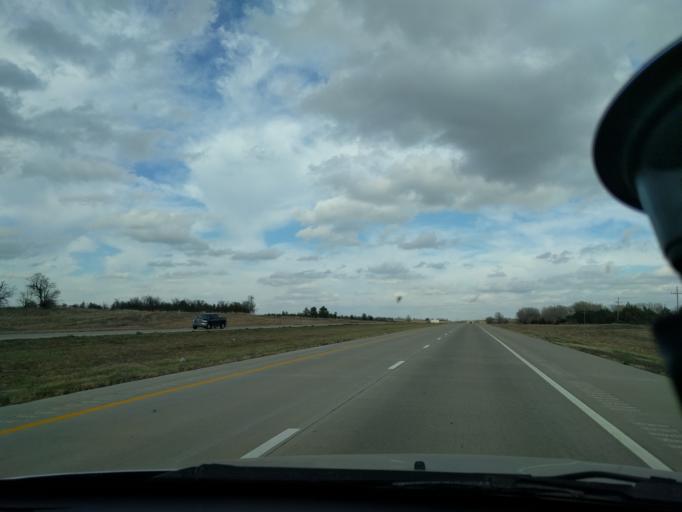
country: US
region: Kansas
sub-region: Reno County
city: Buhler
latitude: 38.1652
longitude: -97.8313
